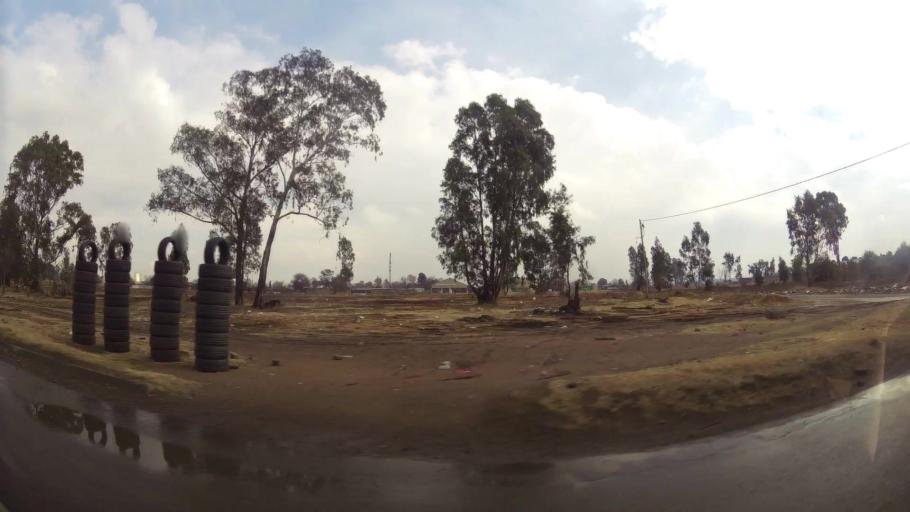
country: ZA
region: Gauteng
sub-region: Sedibeng District Municipality
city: Vereeniging
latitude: -26.6770
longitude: 27.9178
